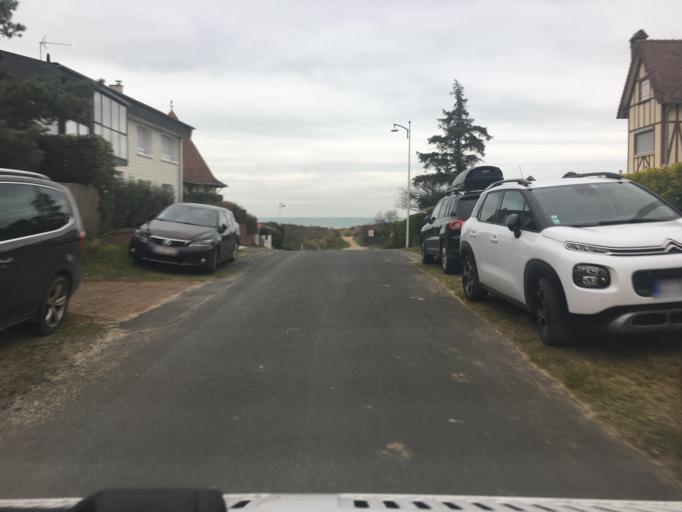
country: FR
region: Lower Normandy
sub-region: Departement du Calvados
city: Merville-Franceville-Plage
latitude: 49.2842
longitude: -0.2083
